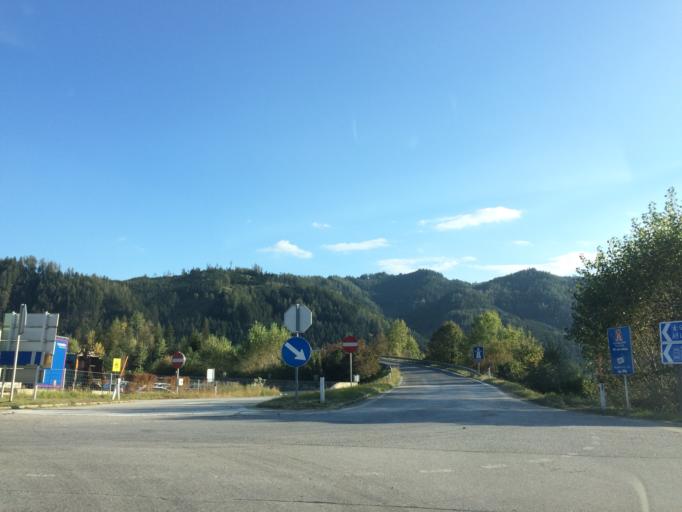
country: AT
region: Styria
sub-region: Politischer Bezirk Leoben
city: Sankt Michael in Obersteiermark
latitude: 47.3386
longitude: 15.0050
